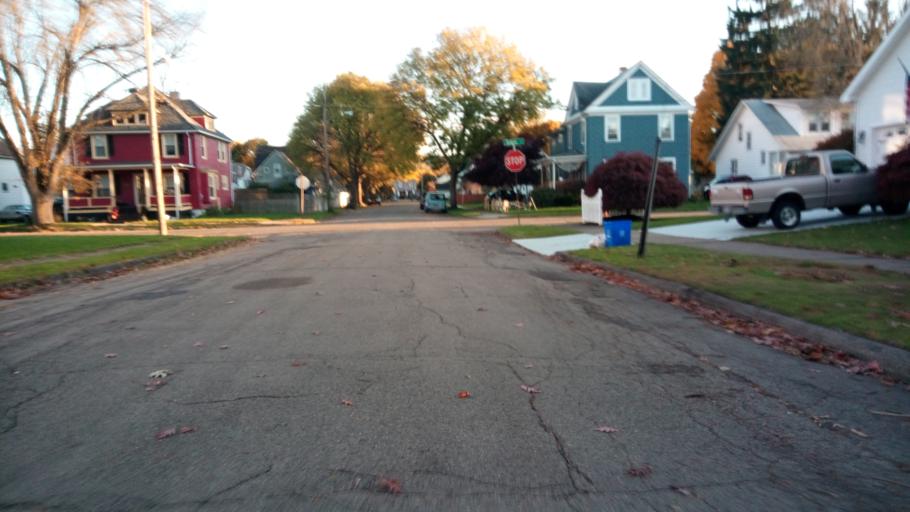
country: US
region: New York
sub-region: Chemung County
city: Elmira
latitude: 42.0718
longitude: -76.8082
